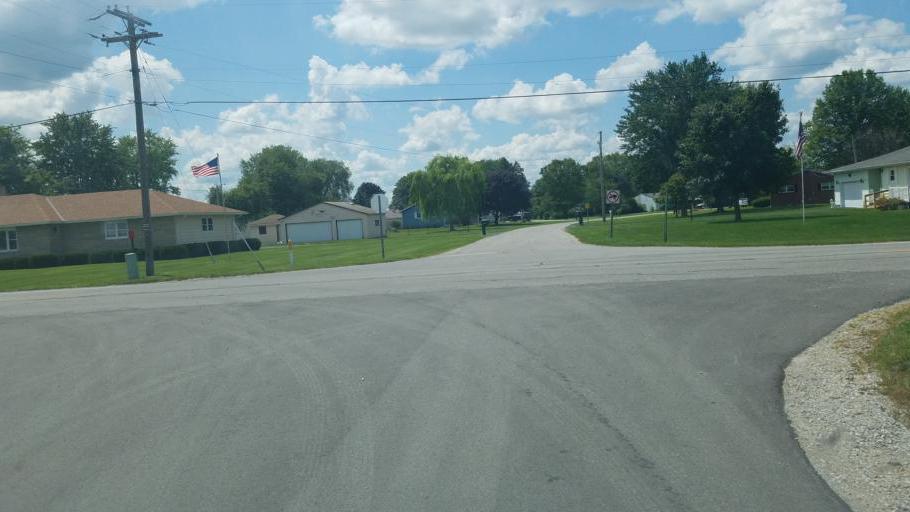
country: US
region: Ohio
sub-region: Marion County
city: Marion
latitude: 40.6155
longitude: -83.0732
